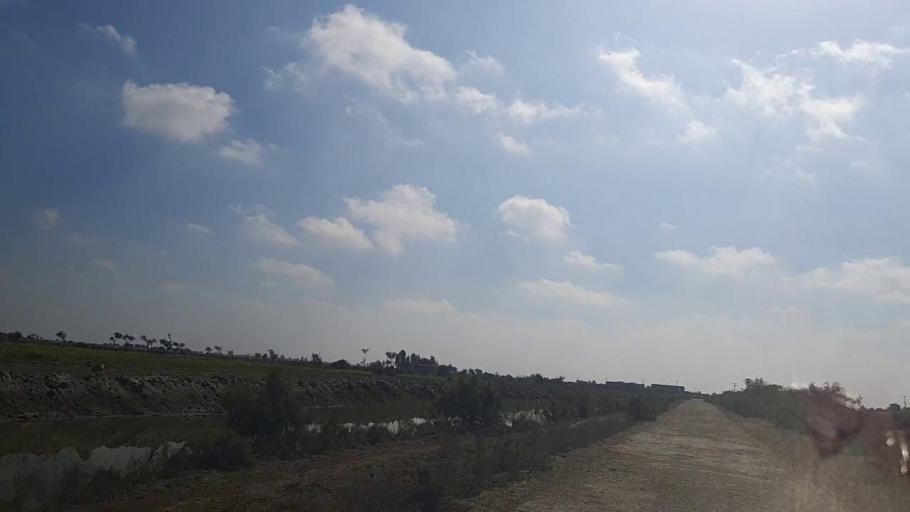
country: PK
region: Sindh
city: Sanghar
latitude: 26.0506
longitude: 69.0045
